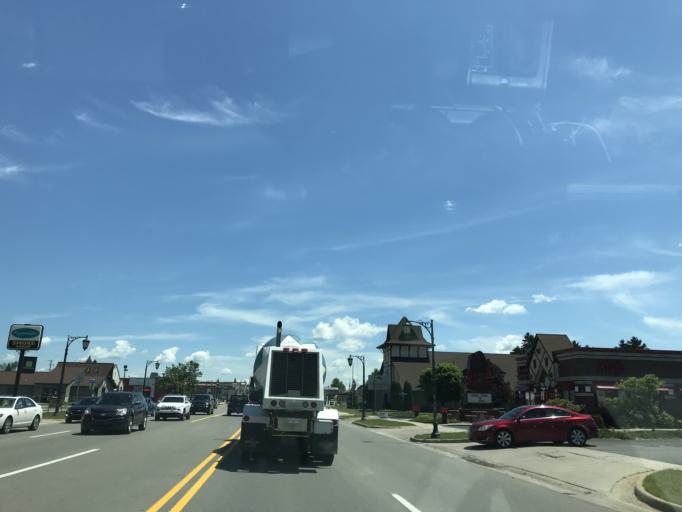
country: US
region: Michigan
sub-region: Otsego County
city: Gaylord
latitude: 45.0274
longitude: -84.6821
